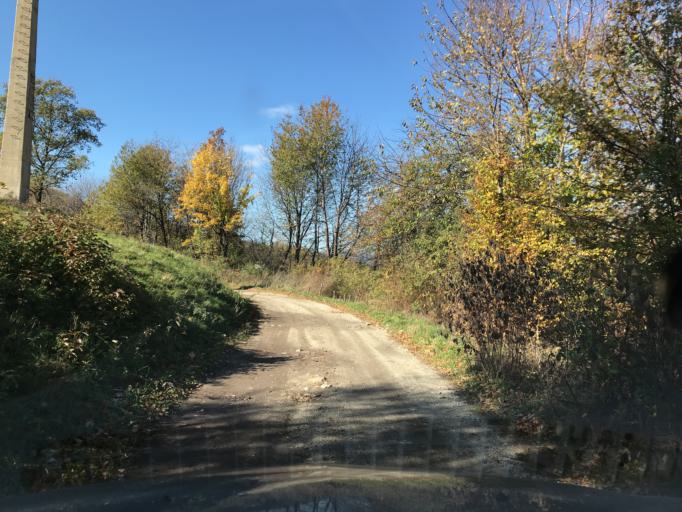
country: BA
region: Federation of Bosnia and Herzegovina
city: Travnik
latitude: 44.2218
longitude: 17.6494
